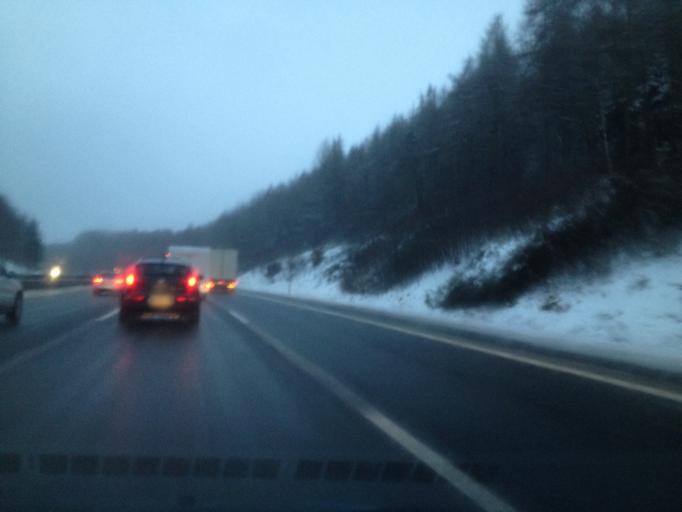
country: DE
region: Rheinland-Pfalz
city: Niederfell
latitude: 50.2784
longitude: 7.5058
